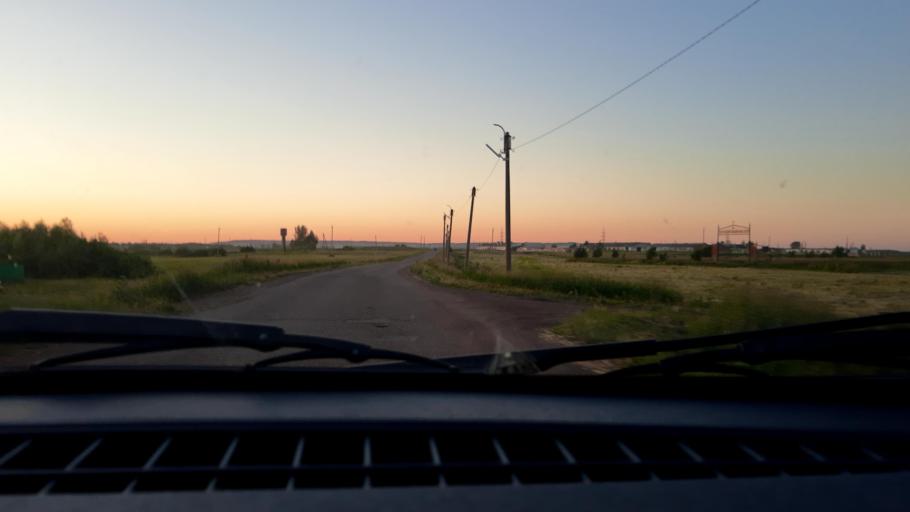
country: RU
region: Bashkortostan
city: Asanovo
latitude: 54.8930
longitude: 55.6253
